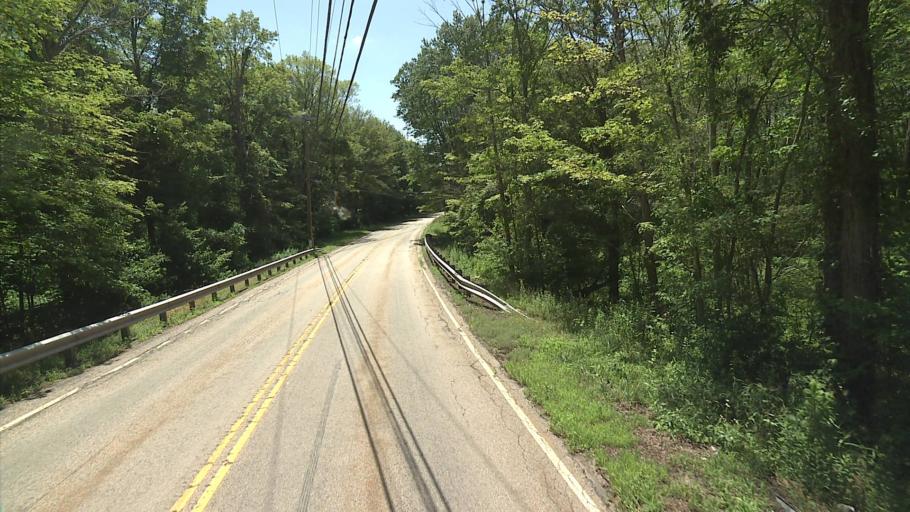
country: US
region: Connecticut
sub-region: Middlesex County
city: East Haddam
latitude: 41.4695
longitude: -72.4176
